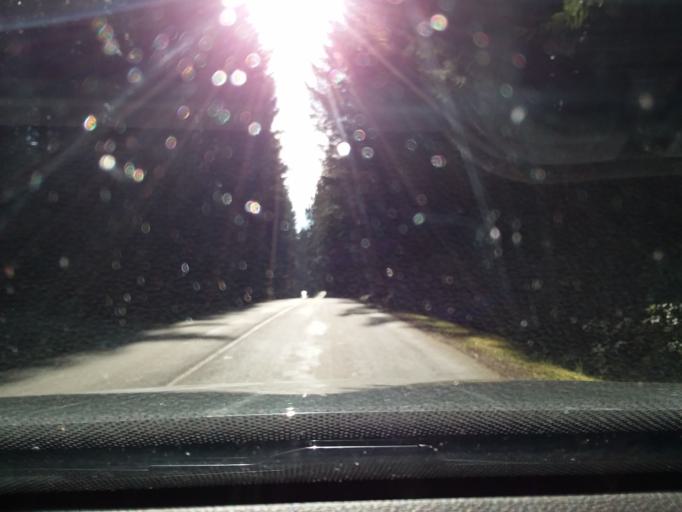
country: CA
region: British Columbia
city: North Saanich
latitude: 48.9176
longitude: -123.4331
